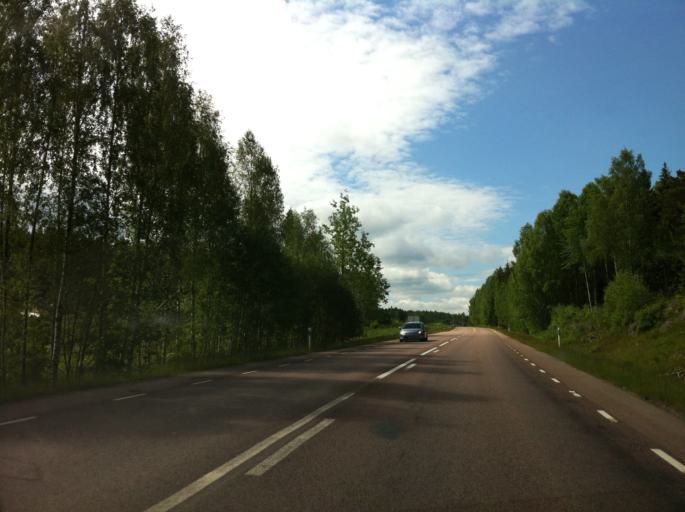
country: SE
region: Vaermland
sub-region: Karlstads Kommun
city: Valberg
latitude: 59.3844
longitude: 13.1727
